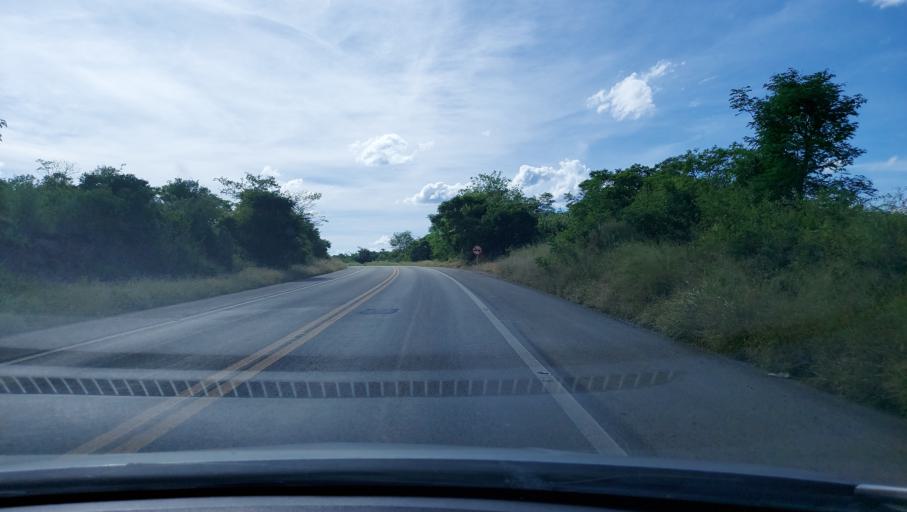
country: BR
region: Bahia
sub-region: Seabra
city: Seabra
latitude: -12.4583
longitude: -41.6270
